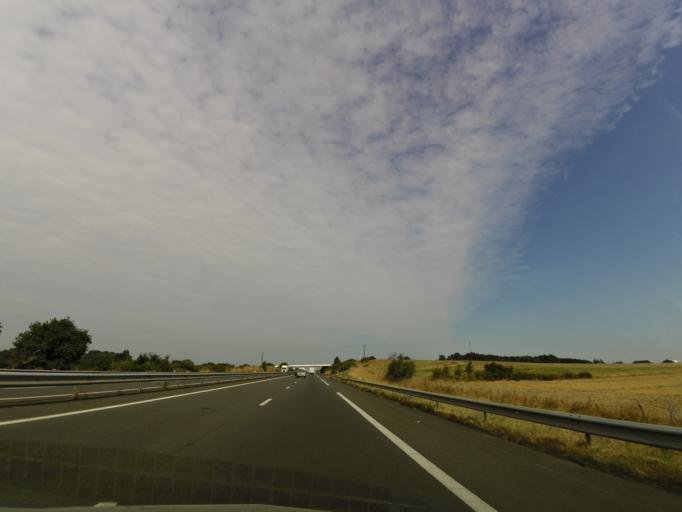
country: FR
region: Pays de la Loire
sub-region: Departement de la Loire-Atlantique
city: Le Bignon
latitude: 47.0859
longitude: -1.4529
